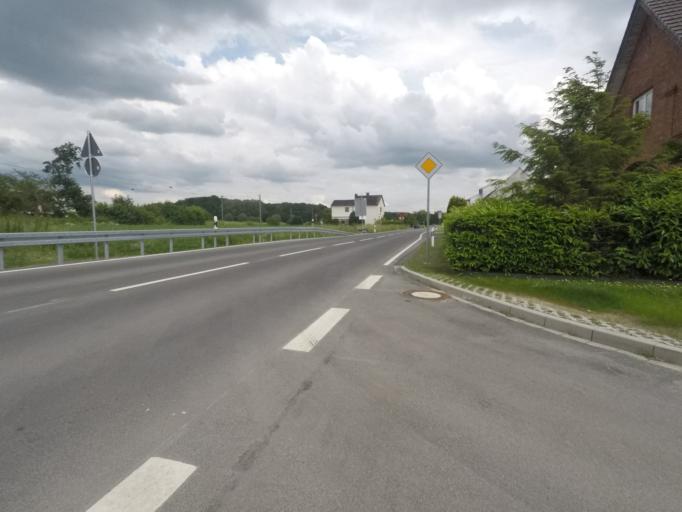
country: DE
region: North Rhine-Westphalia
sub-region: Regierungsbezirk Detmold
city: Rodinghausen
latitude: 52.1975
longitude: 8.4799
